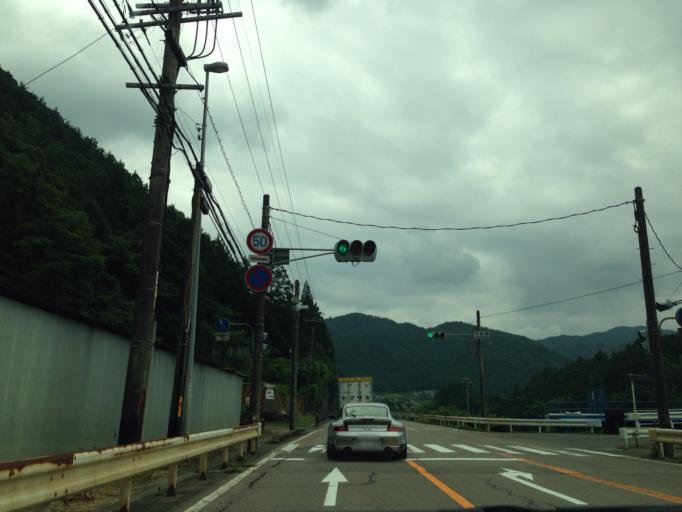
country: JP
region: Gifu
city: Minokamo
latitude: 35.6207
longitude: 137.1620
